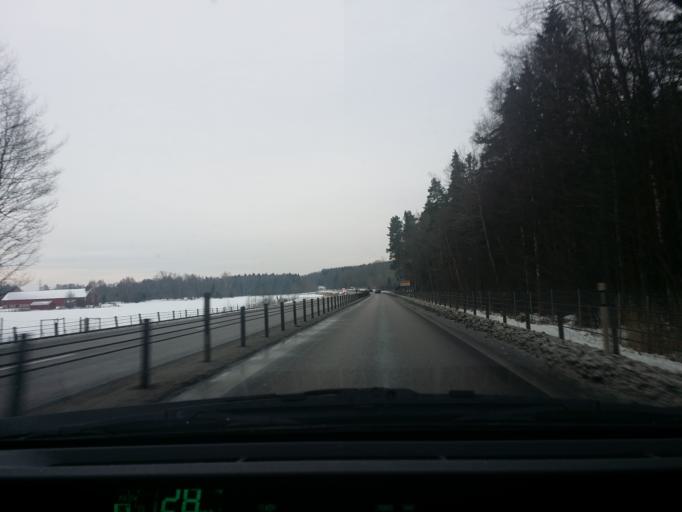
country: SE
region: Vaestra Goetaland
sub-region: Skovde Kommun
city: Stopen
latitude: 58.5045
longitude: 13.8399
